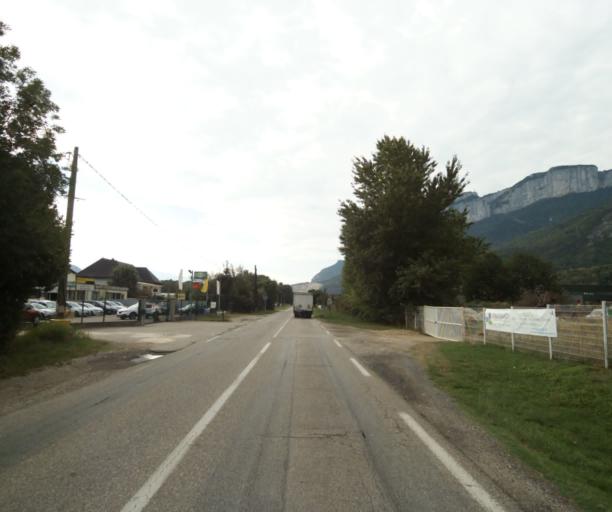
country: FR
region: Rhone-Alpes
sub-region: Departement de l'Isere
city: Noyarey
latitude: 45.2583
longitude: 5.6268
